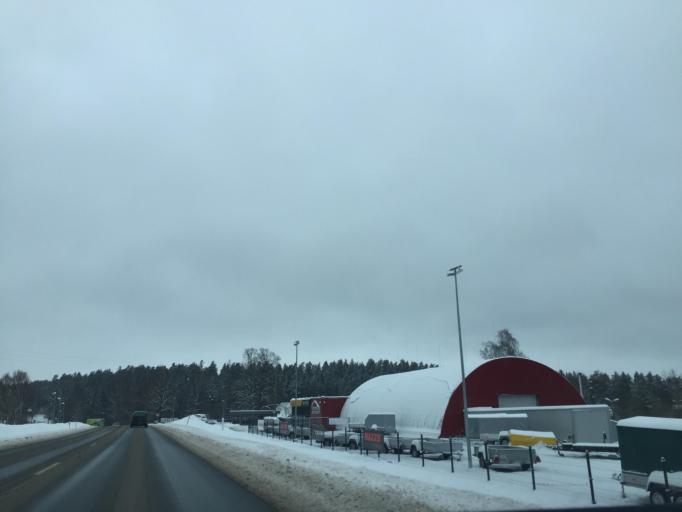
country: LV
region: Smiltene
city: Smiltene
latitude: 57.4154
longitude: 25.9321
